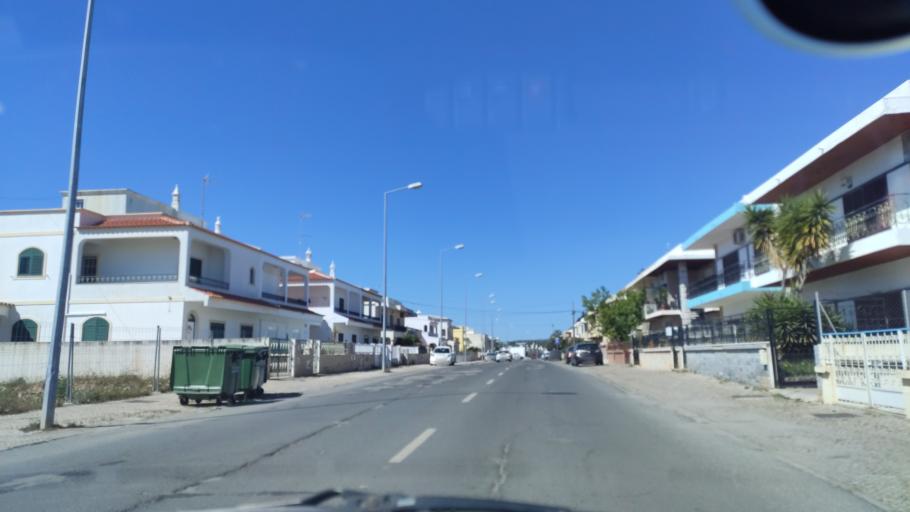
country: PT
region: Faro
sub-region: Olhao
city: Olhao
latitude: 37.0359
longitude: -7.8485
